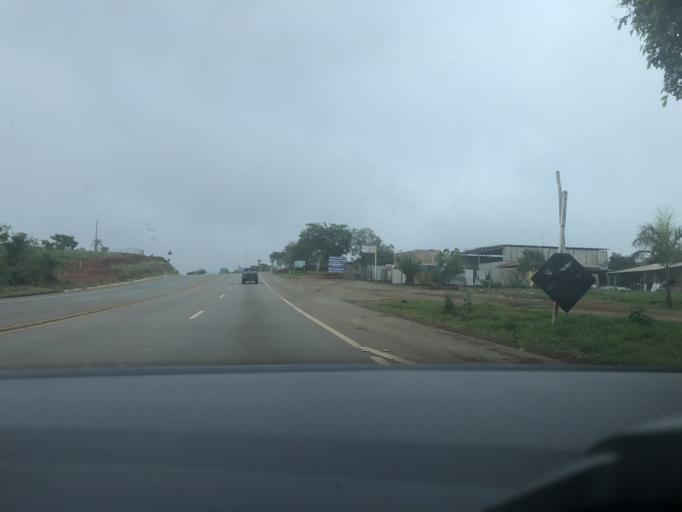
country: BR
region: Minas Gerais
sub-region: Congonhas
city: Congonhas
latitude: -20.6136
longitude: -43.9205
